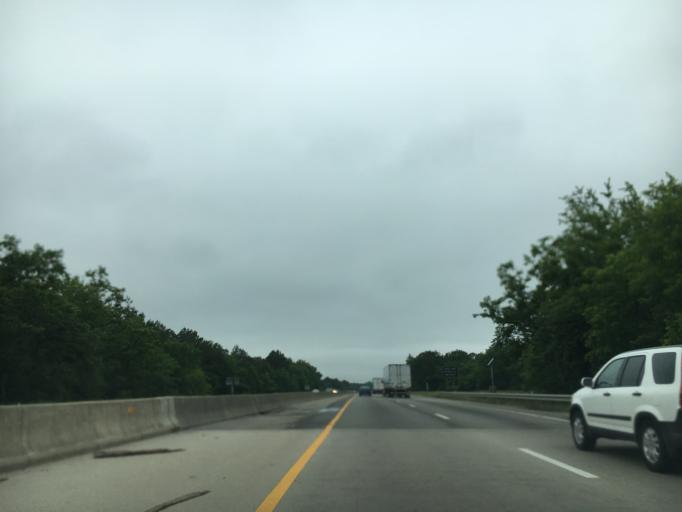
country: US
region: Virginia
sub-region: Chesterfield County
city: Matoaca
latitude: 37.1992
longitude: -77.4545
